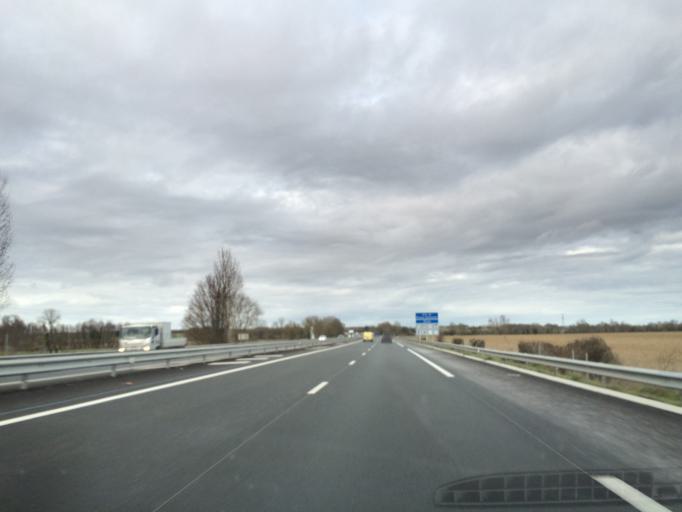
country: FR
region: Poitou-Charentes
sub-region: Departement des Deux-Sevres
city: Beauvoir-sur-Niort
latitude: 46.1502
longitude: -0.5204
